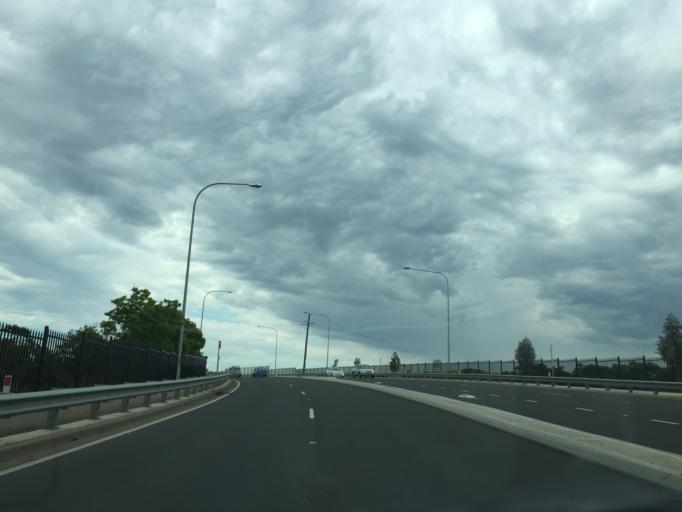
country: AU
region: New South Wales
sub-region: Blacktown
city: Doonside
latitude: -33.7640
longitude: 150.8628
